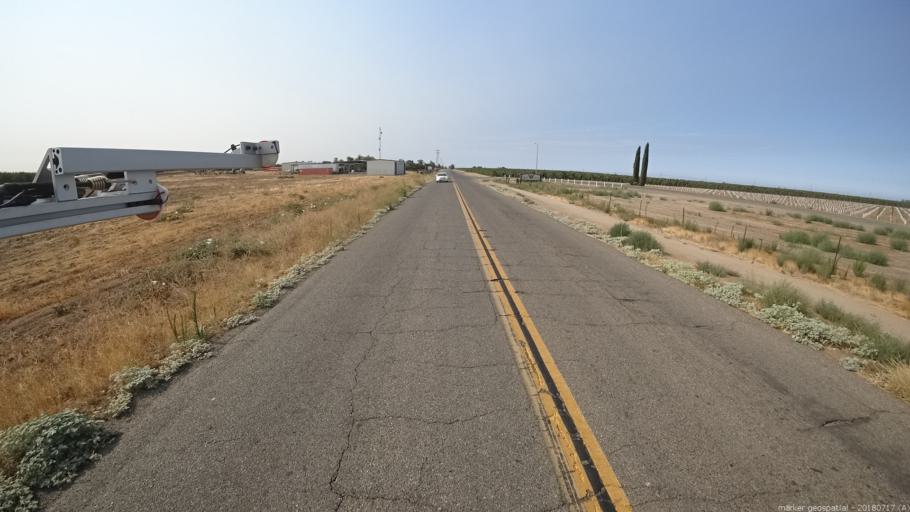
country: US
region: California
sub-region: Madera County
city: Madera Acres
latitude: 37.0698
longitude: -120.1108
